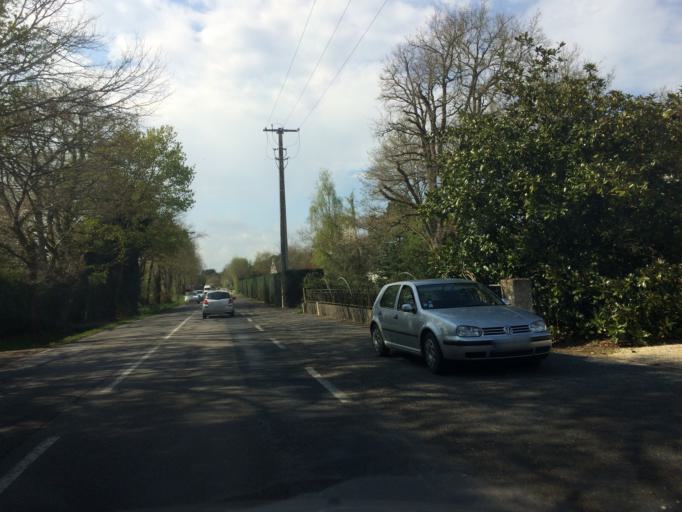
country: FR
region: Pays de la Loire
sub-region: Departement de la Loire-Atlantique
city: Suce-sur-Erdre
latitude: 47.3324
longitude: -1.5150
